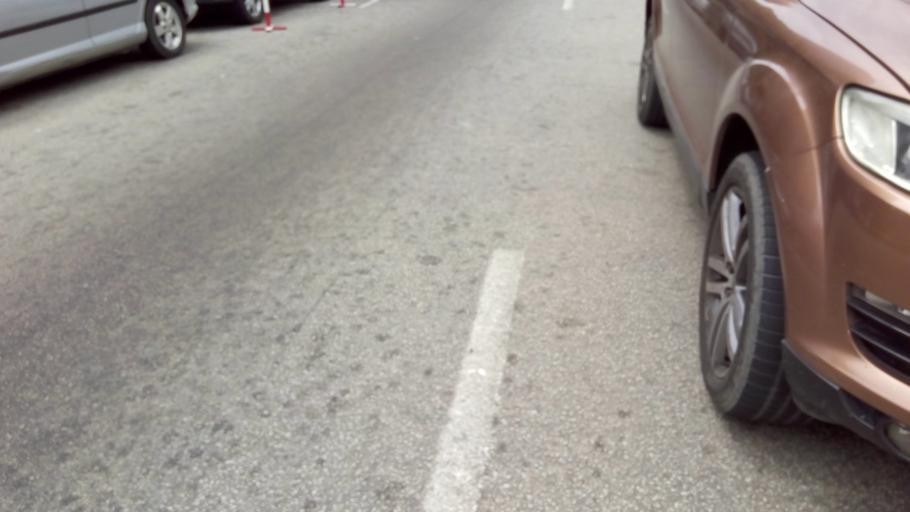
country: CI
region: Lagunes
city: Abidjan
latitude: 5.3252
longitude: -4.0184
